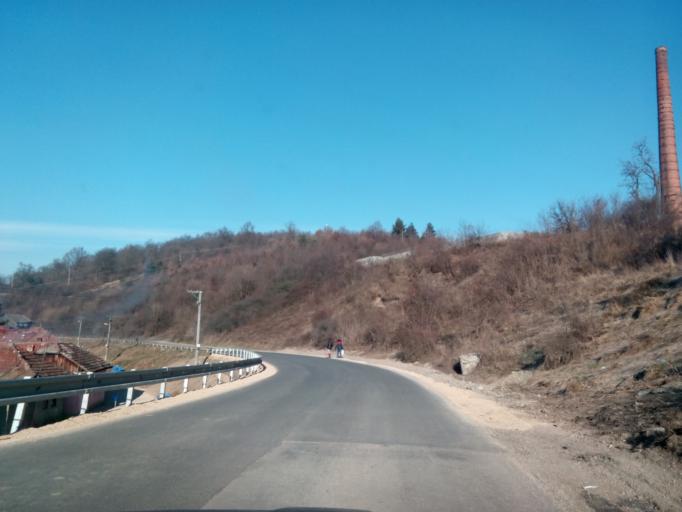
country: SK
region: Kosicky
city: Moldava nad Bodvou
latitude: 48.6858
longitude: 20.9709
